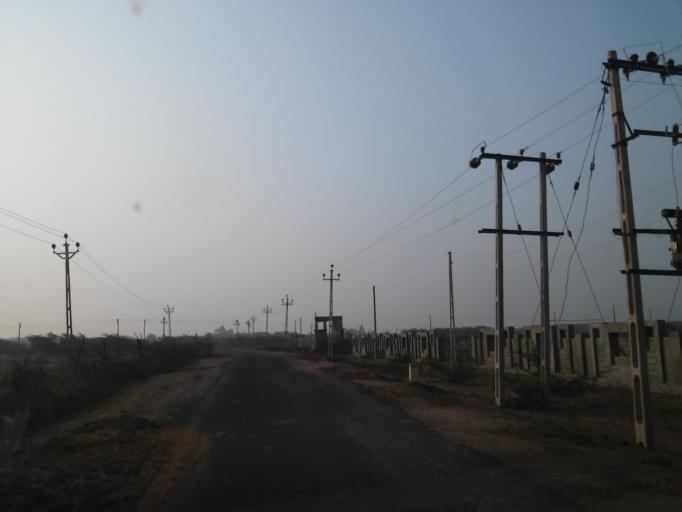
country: IN
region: Gujarat
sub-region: Kachchh
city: Mandvi
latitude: 22.8200
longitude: 69.3895
